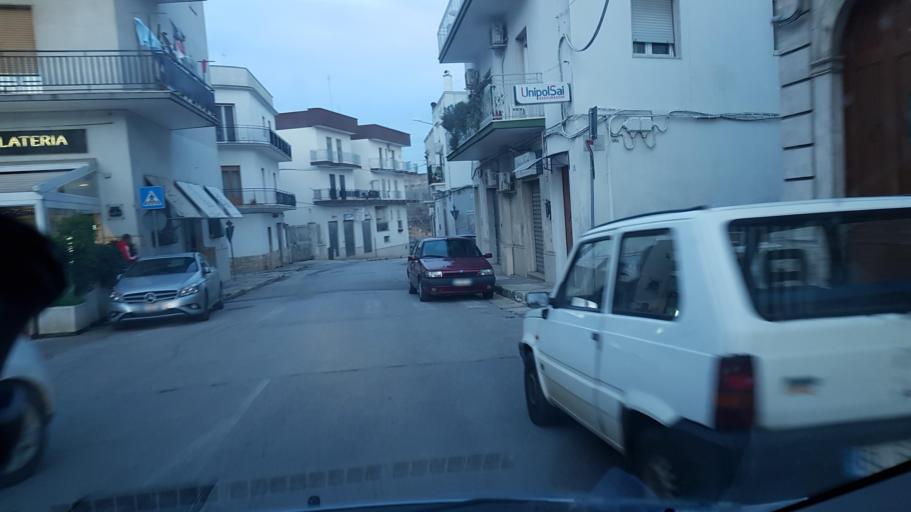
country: IT
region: Apulia
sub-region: Provincia di Brindisi
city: Ceglie Messapica
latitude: 40.6451
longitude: 17.5209
